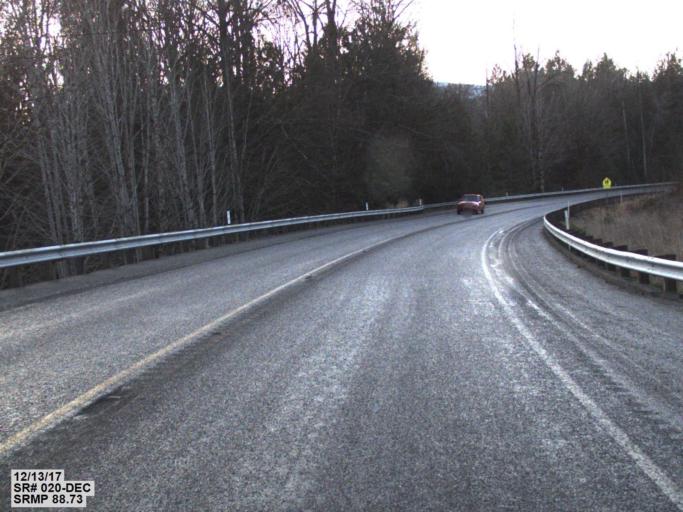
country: US
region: Washington
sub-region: Snohomish County
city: Darrington
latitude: 48.5362
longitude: -121.7550
